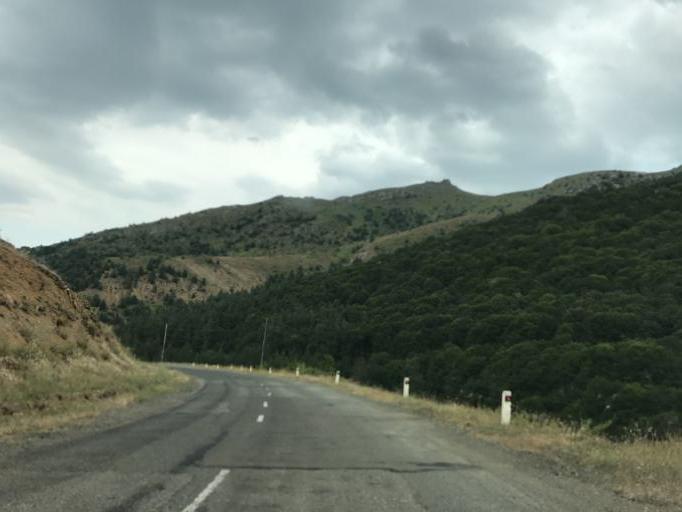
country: AZ
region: Susa
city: Shushi
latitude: 39.7036
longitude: 46.6525
